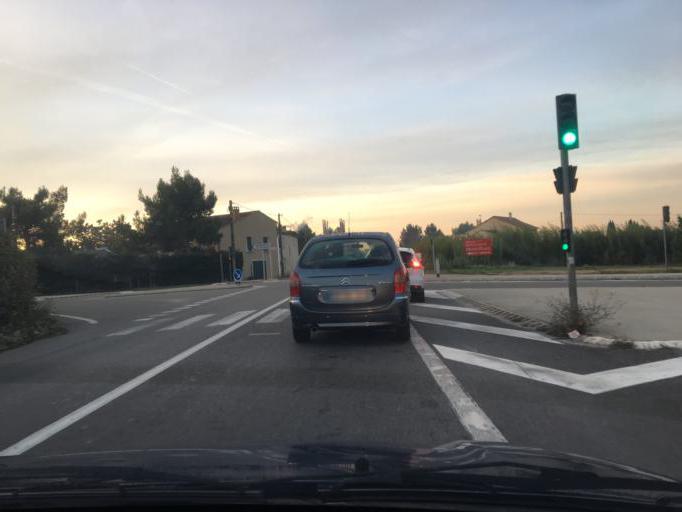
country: FR
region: Provence-Alpes-Cote d'Azur
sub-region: Departement du Vaucluse
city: Pernes-les-Fontaines
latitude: 44.0226
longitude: 5.0362
